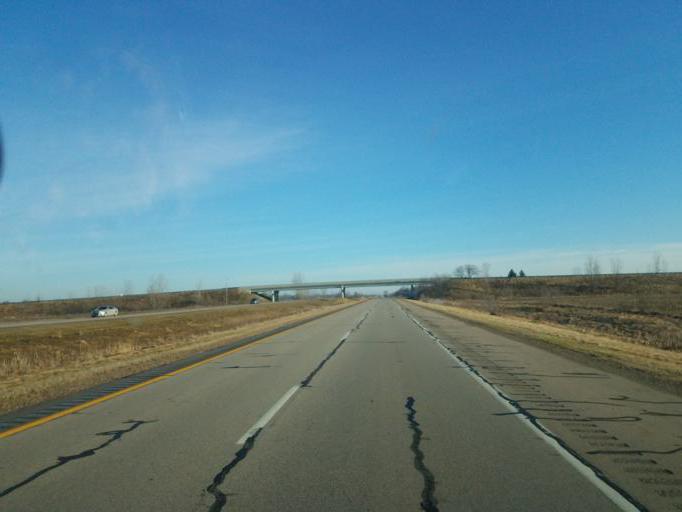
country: US
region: Michigan
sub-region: Clinton County
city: Saint Johns
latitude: 42.9552
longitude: -84.5185
